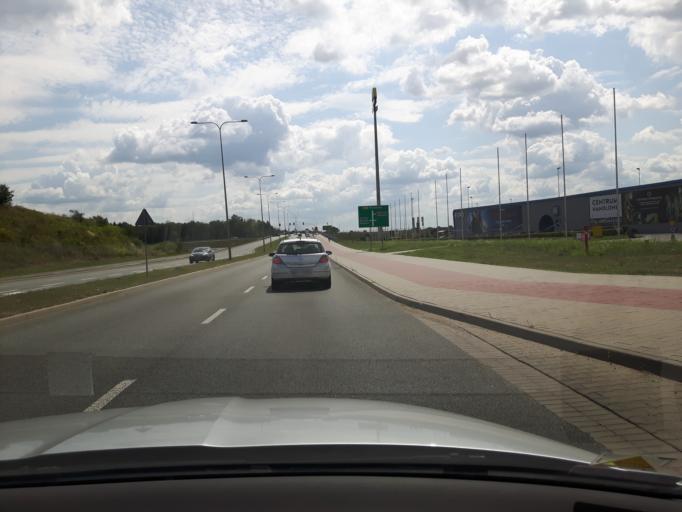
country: PL
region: Masovian Voivodeship
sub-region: Powiat pruszkowski
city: Nadarzyn
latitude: 52.1097
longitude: 20.8341
